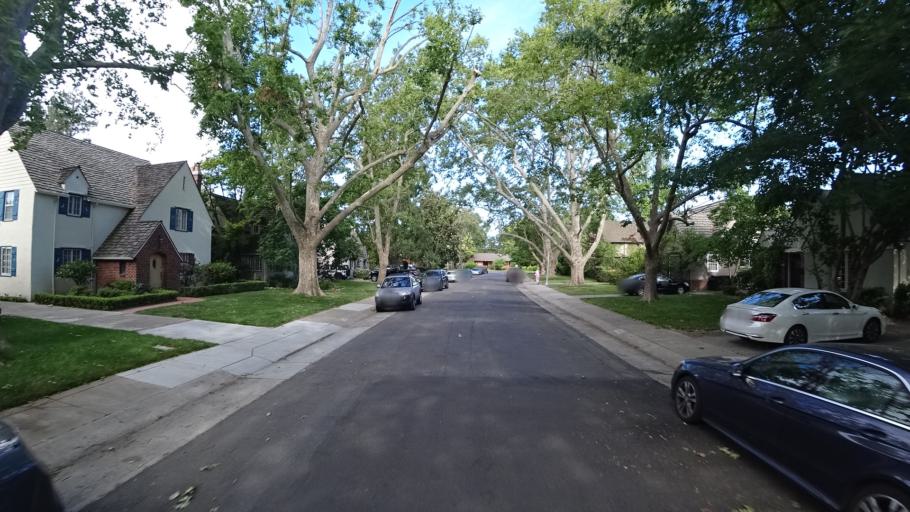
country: US
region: California
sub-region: Sacramento County
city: Sacramento
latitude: 38.5530
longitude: -121.5031
